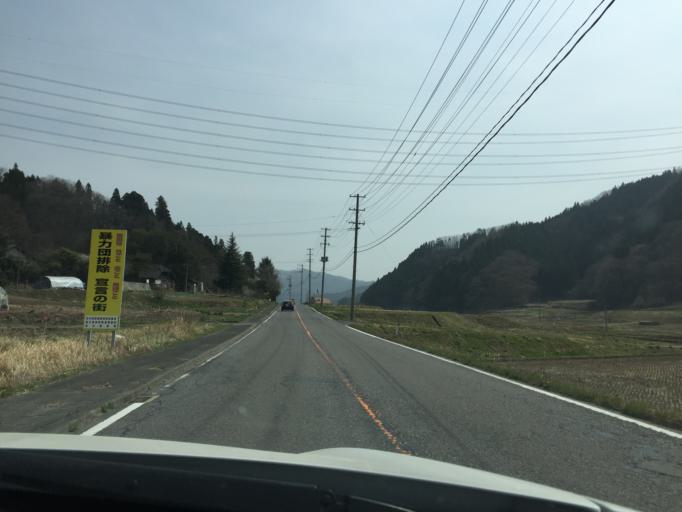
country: JP
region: Fukushima
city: Ishikawa
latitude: 37.1032
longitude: 140.5087
